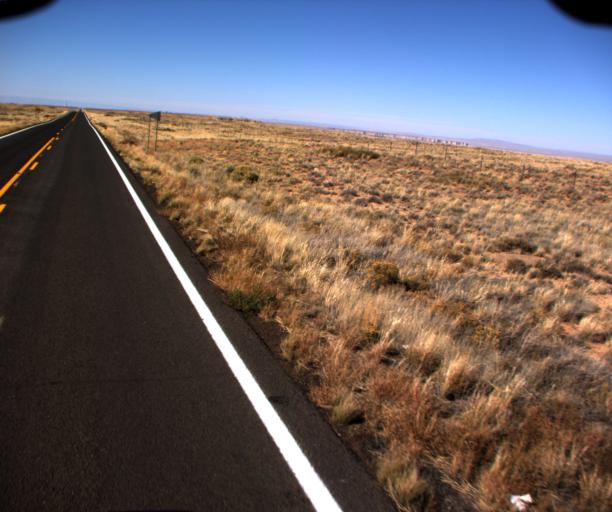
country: US
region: Arizona
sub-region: Coconino County
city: Tuba City
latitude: 35.9708
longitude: -110.9636
